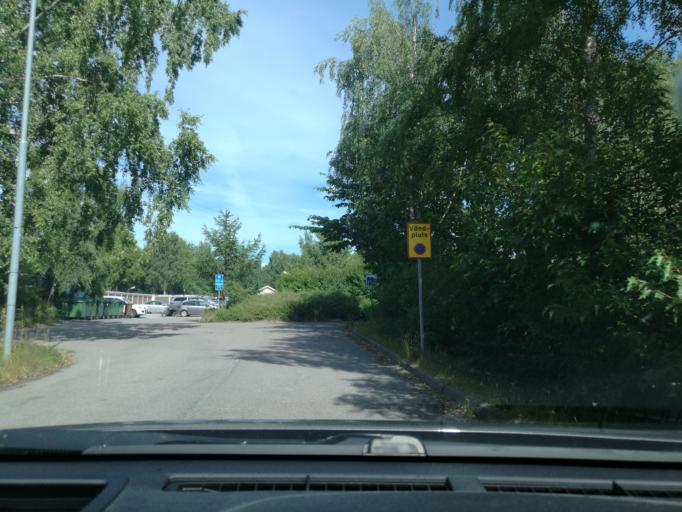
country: SE
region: Stockholm
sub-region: Upplands Vasby Kommun
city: Upplands Vaesby
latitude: 59.4856
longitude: 17.8924
